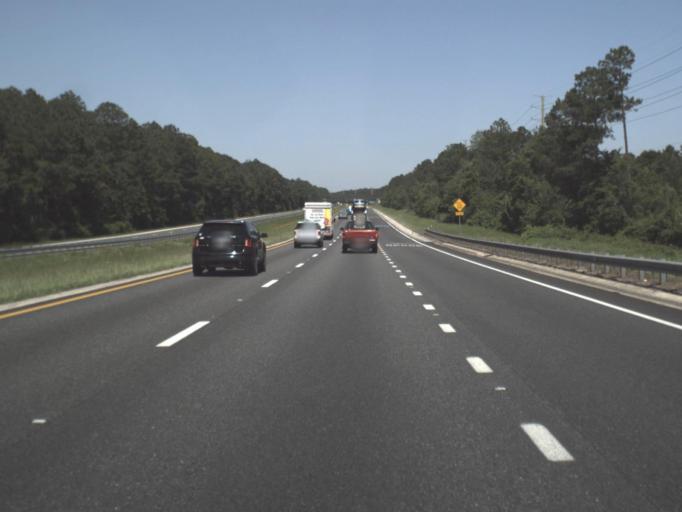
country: US
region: Florida
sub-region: Duval County
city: Baldwin
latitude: 30.2893
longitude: -81.9765
